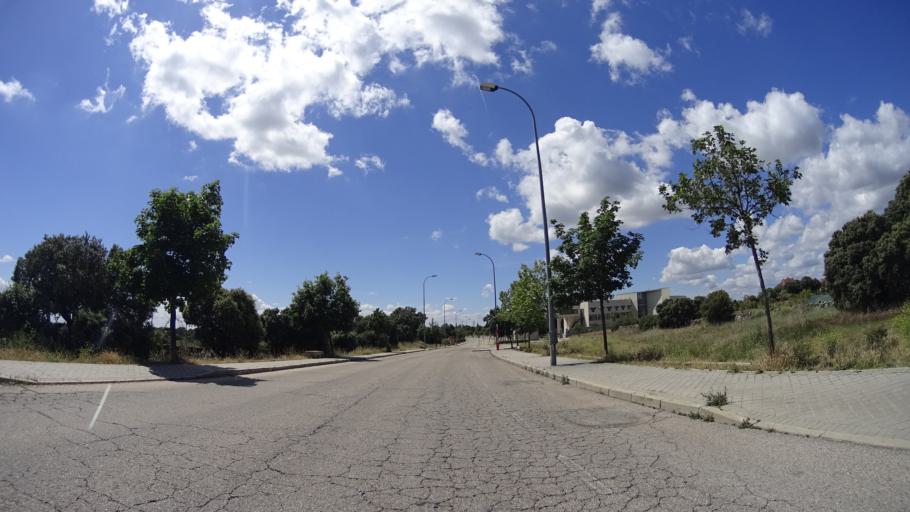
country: ES
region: Madrid
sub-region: Provincia de Madrid
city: Colmenarejo
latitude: 40.5476
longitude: -4.0112
